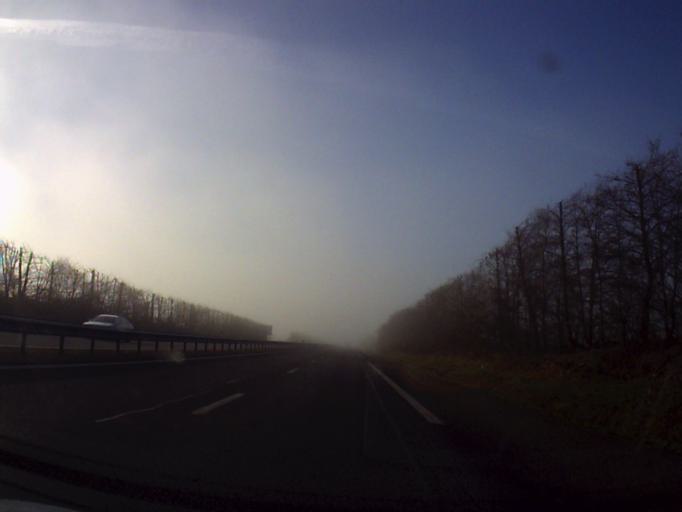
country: FR
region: Brittany
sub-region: Departement d'Ille-et-Vilaine
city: Plelan-le-Grand
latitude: 47.9861
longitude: -2.0980
